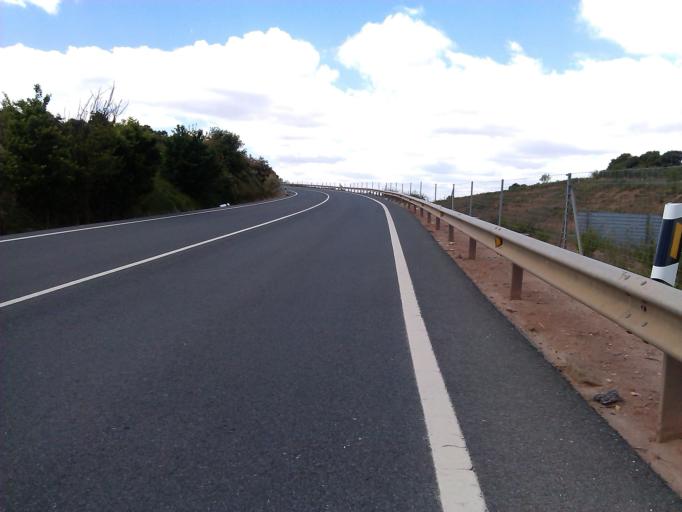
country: ES
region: La Rioja
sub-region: Provincia de La Rioja
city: Ventosa
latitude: 42.4173
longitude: -2.6387
